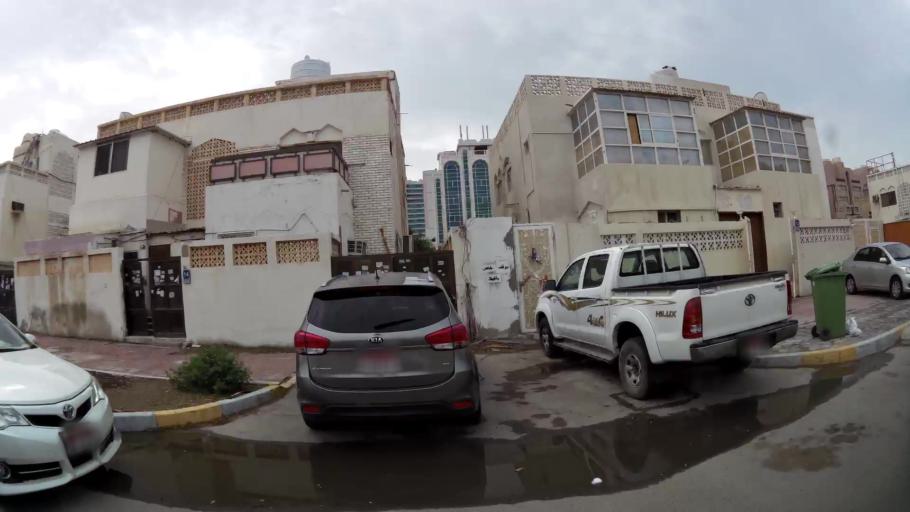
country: AE
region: Abu Dhabi
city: Abu Dhabi
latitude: 24.4348
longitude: 54.4363
